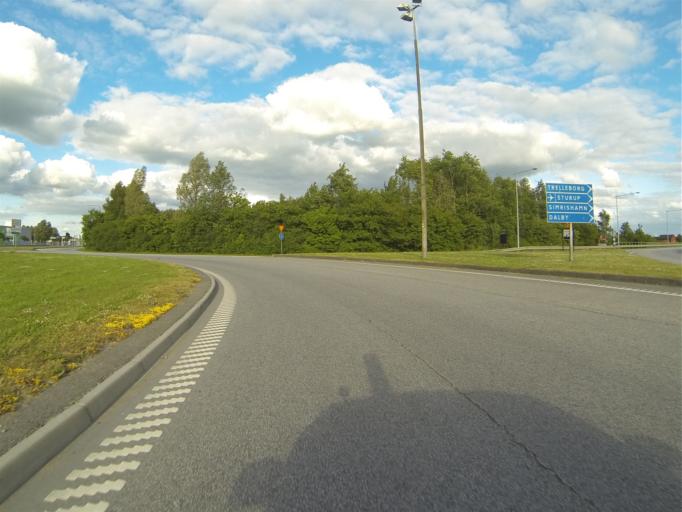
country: SE
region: Skane
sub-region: Staffanstorps Kommun
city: Staffanstorp
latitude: 55.6416
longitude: 13.2329
